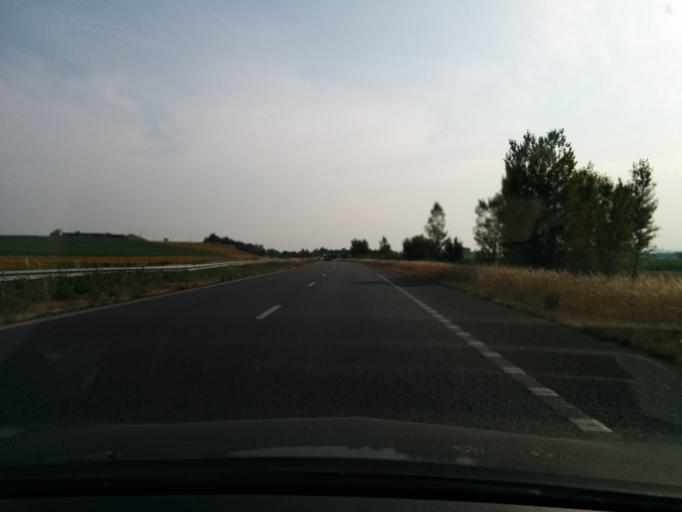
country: FR
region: Midi-Pyrenees
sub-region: Departement du Tarn
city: Lisle-sur-Tarn
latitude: 43.8395
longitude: 1.8408
